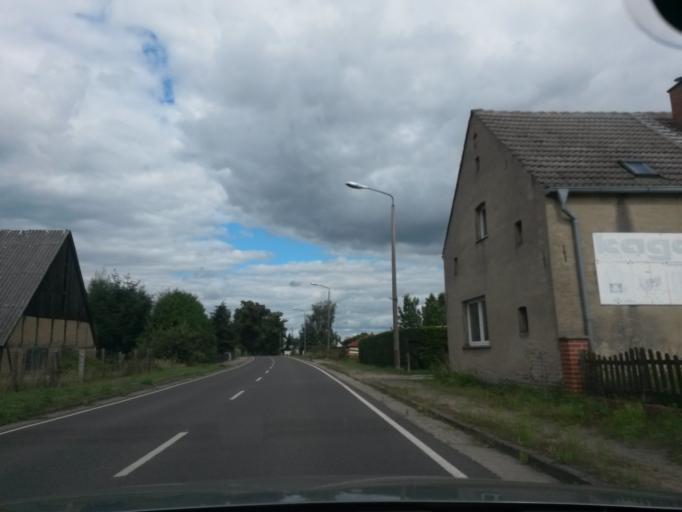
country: DE
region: Brandenburg
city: Chorin
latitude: 52.9373
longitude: 13.9330
